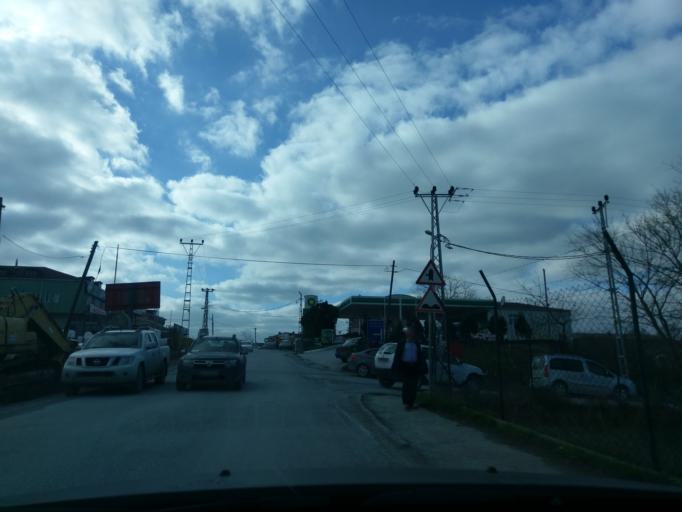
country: TR
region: Istanbul
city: Durusu
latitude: 41.2653
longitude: 28.6872
